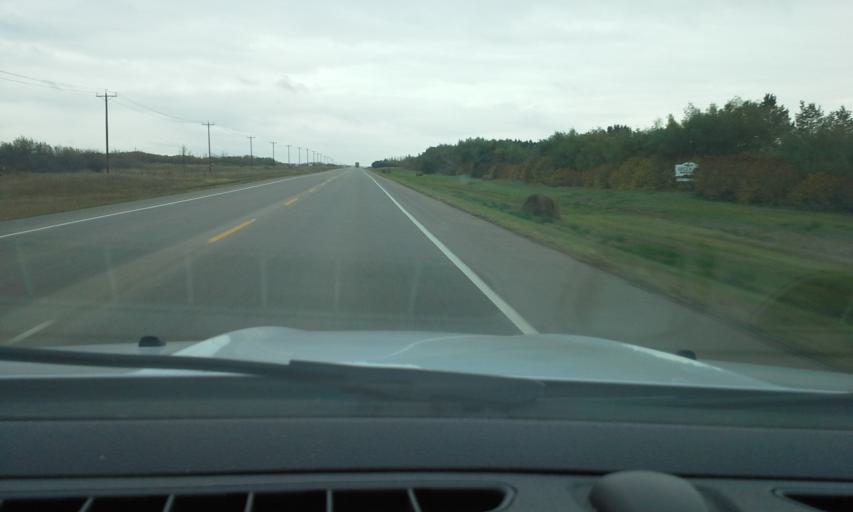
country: CA
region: Saskatchewan
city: Lloydminster
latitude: 53.2780
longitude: -109.8416
